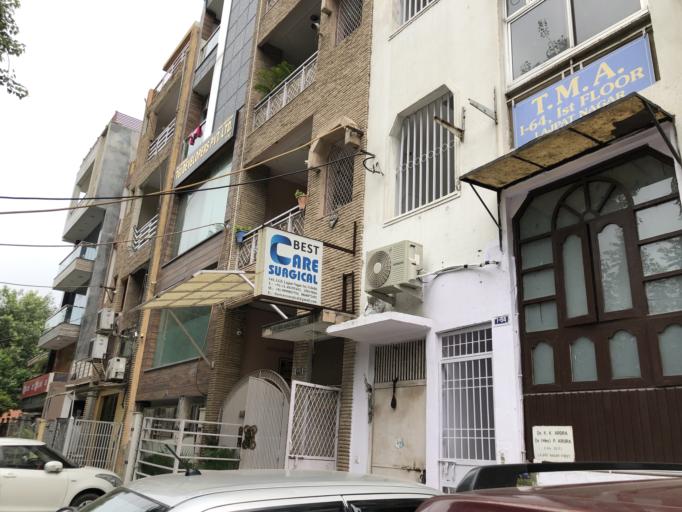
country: IN
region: NCT
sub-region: New Delhi
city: New Delhi
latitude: 28.5787
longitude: 77.2450
